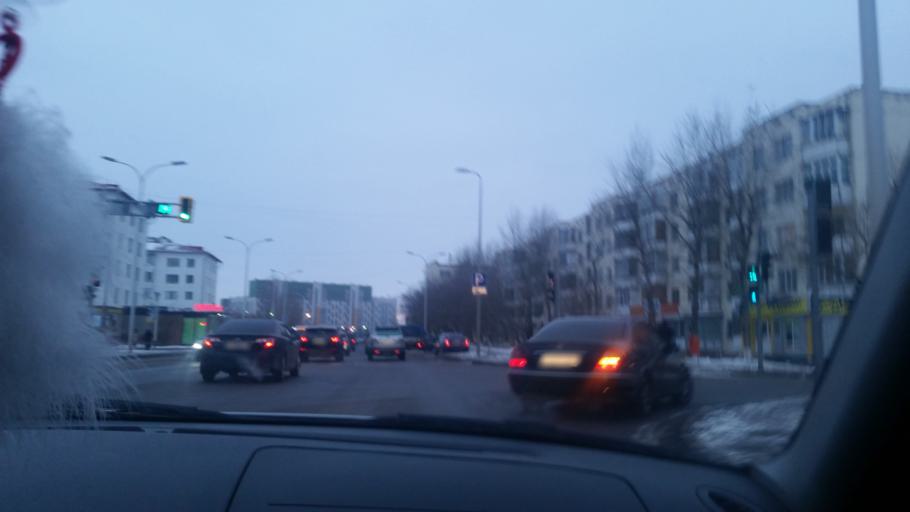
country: KZ
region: Astana Qalasy
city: Astana
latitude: 51.1461
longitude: 71.4660
